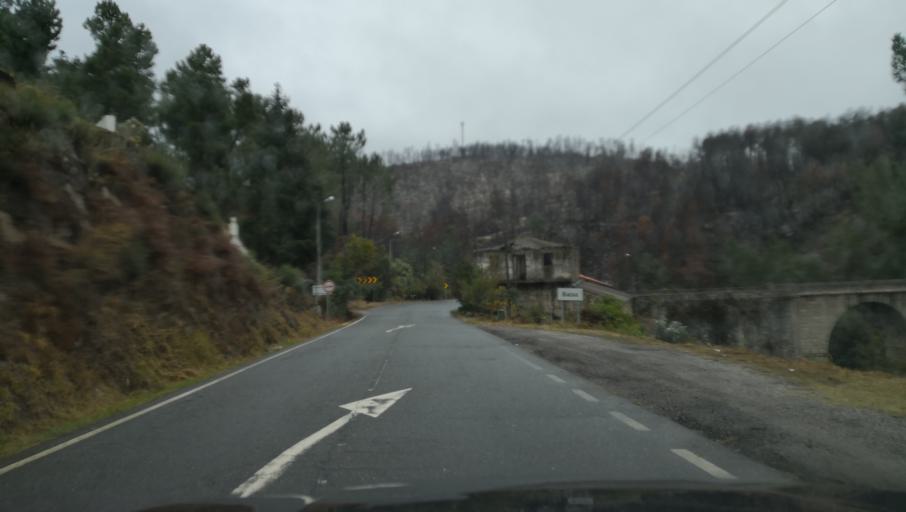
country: PT
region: Vila Real
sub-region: Sabrosa
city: Sabrosa
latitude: 41.3513
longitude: -7.5926
